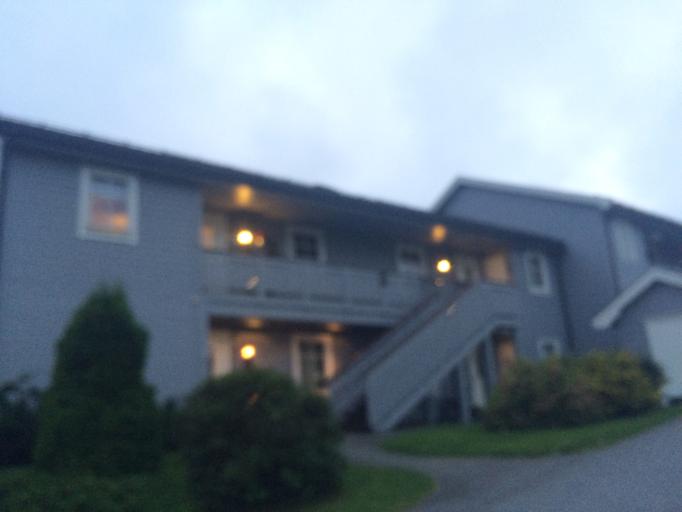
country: NO
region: Akershus
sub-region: Ski
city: Ski
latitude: 59.7184
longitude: 10.8282
